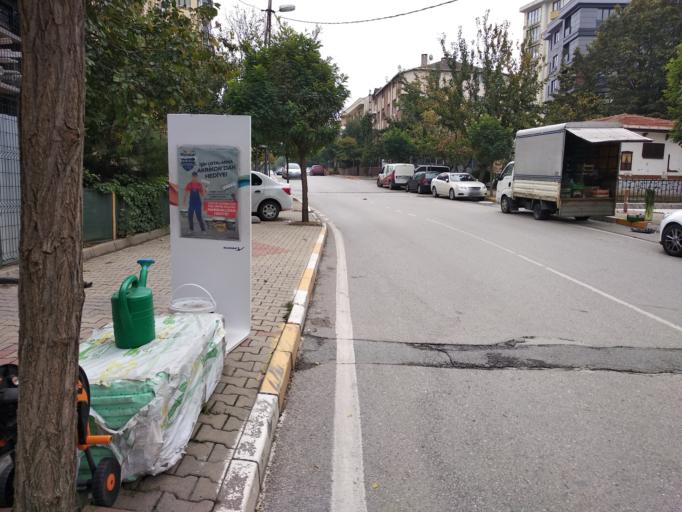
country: TR
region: Istanbul
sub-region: Atasehir
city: Atasehir
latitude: 40.9816
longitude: 29.1212
